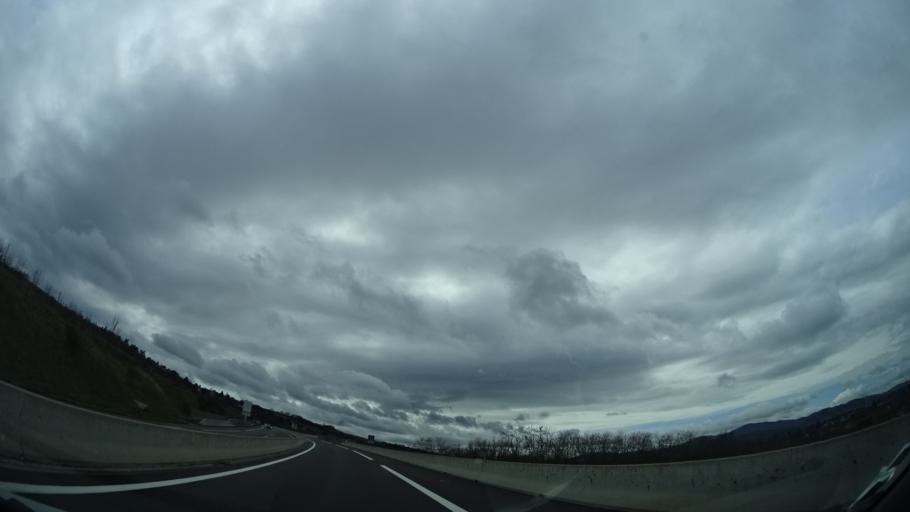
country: FR
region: Rhone-Alpes
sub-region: Departement du Rhone
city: Saint-Germain-Nuelles
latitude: 45.8449
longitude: 4.6406
